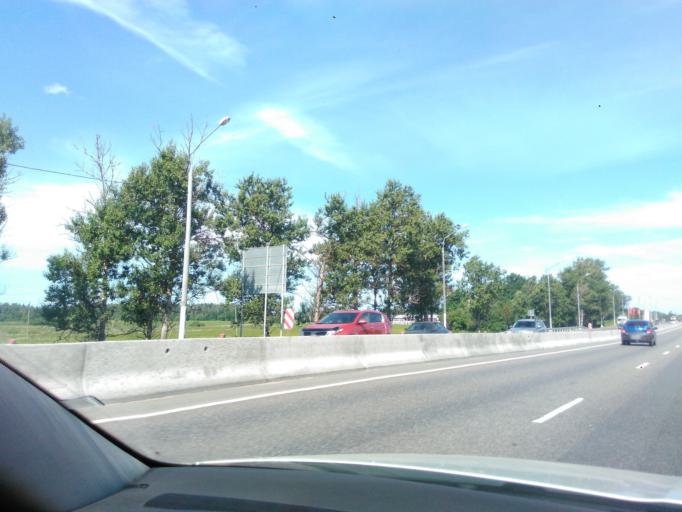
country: RU
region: Moskovskaya
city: Peshki
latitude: 56.1160
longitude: 37.0847
